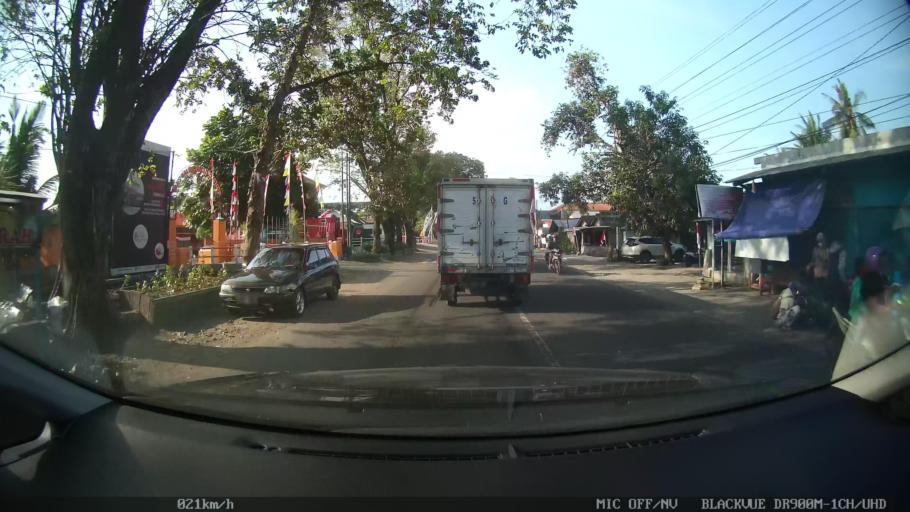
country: ID
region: Daerah Istimewa Yogyakarta
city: Bantul
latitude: -7.9003
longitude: 110.3219
